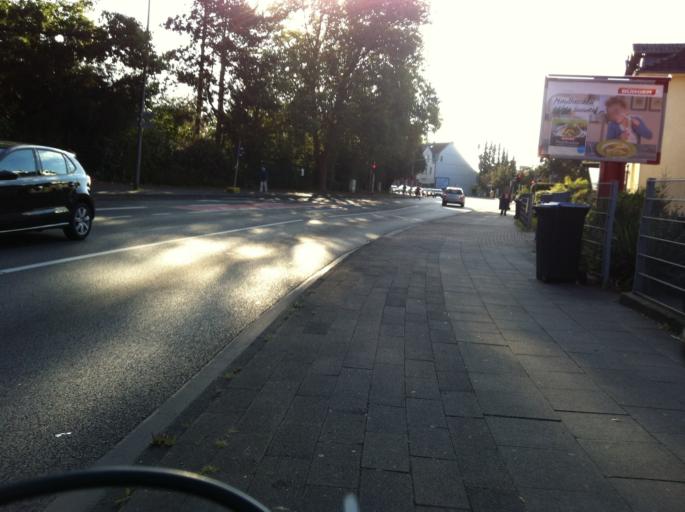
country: DE
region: North Rhine-Westphalia
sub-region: Regierungsbezirk Koln
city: Porz am Rhein
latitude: 50.8819
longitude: 7.0712
